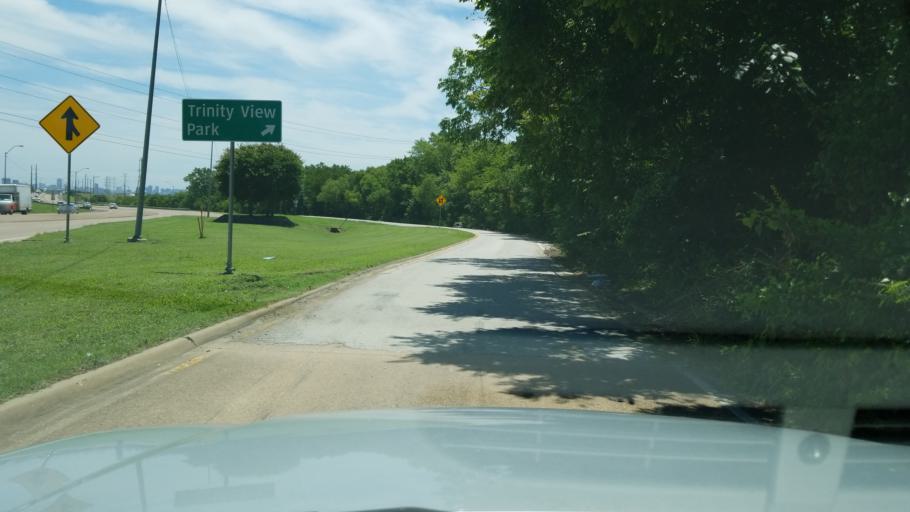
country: US
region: Texas
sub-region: Dallas County
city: Irving
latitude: 32.8093
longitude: -96.9156
